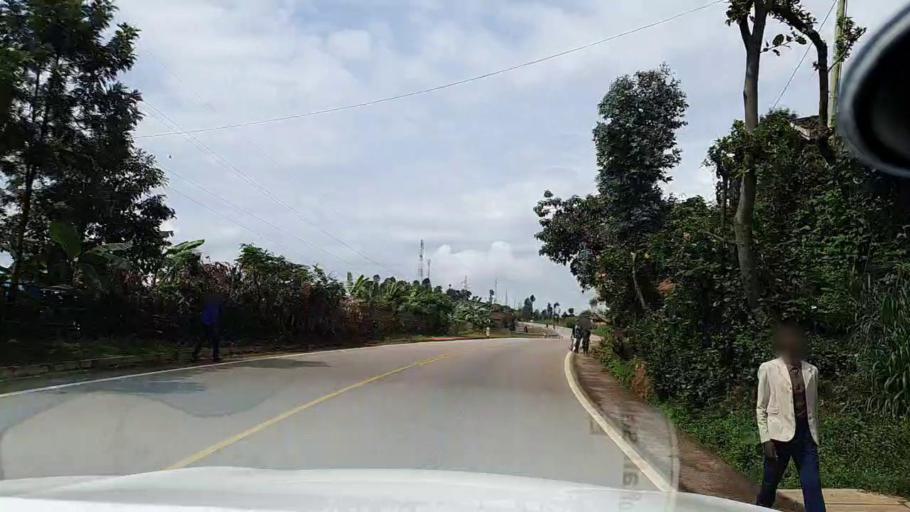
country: RW
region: Southern Province
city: Nzega
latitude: -2.4825
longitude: 29.5343
